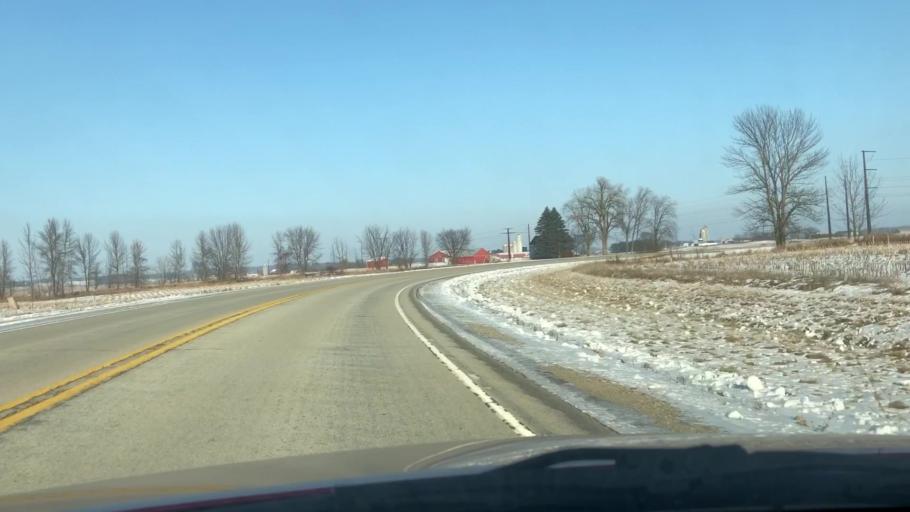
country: US
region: Wisconsin
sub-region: Outagamie County
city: Seymour
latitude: 44.4423
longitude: -88.3605
